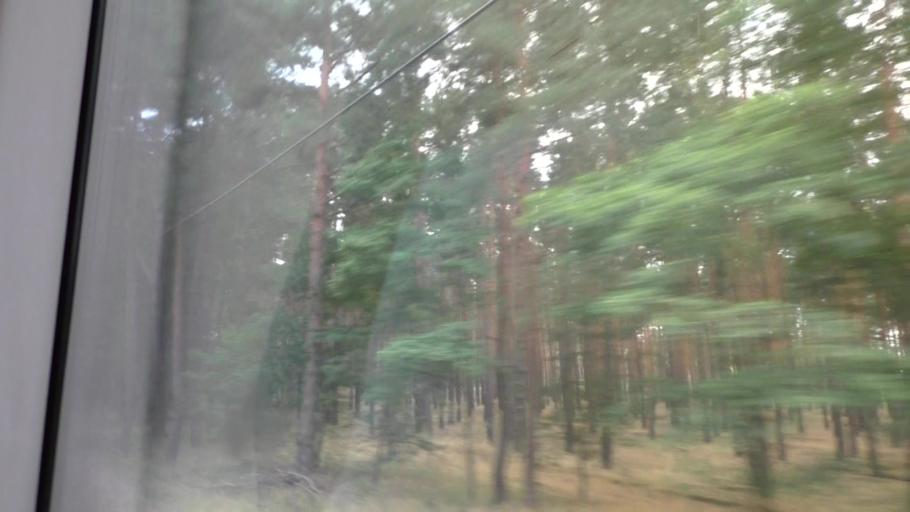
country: DE
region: Brandenburg
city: Storkow
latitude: 52.2628
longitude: 13.8985
